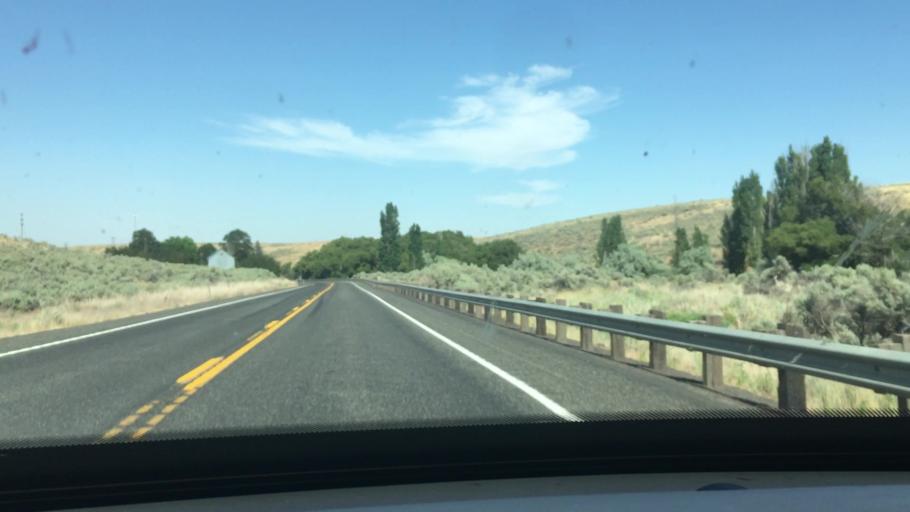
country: US
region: Oregon
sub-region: Sherman County
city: Moro
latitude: 45.5048
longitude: -120.6934
